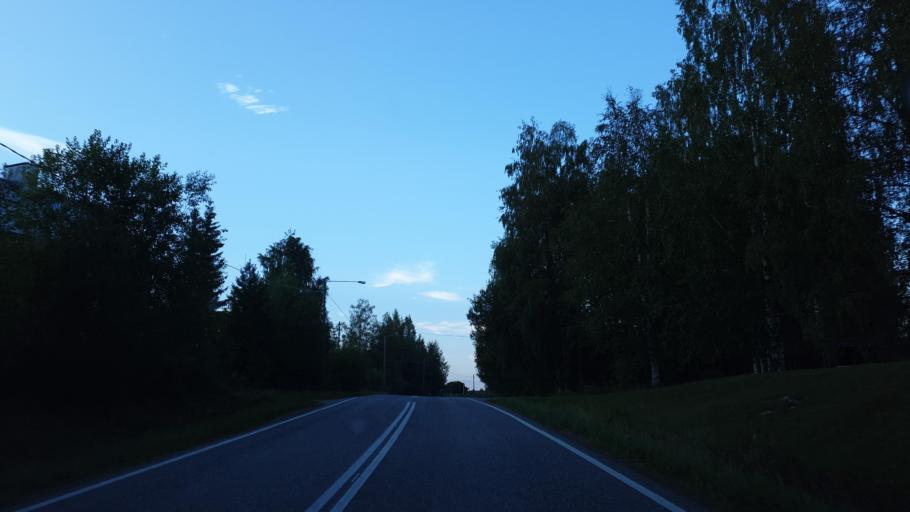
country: FI
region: Northern Savo
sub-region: Koillis-Savo
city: Kaavi
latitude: 62.9703
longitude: 28.7696
